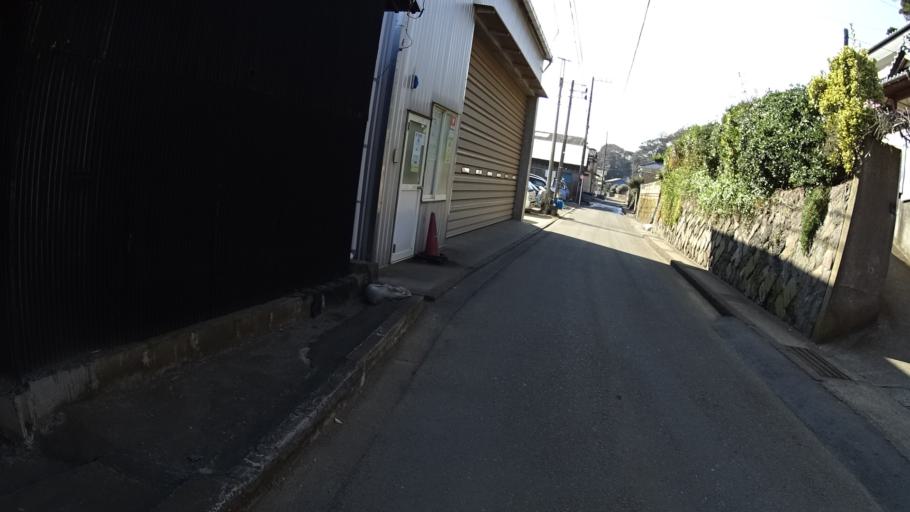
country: JP
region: Kanagawa
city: Miura
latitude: 35.1870
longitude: 139.6225
